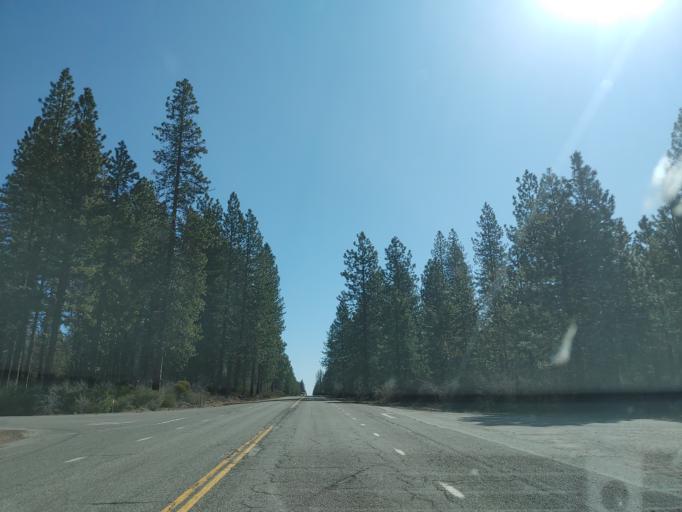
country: US
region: California
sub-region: Siskiyou County
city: McCloud
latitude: 41.2513
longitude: -122.1231
